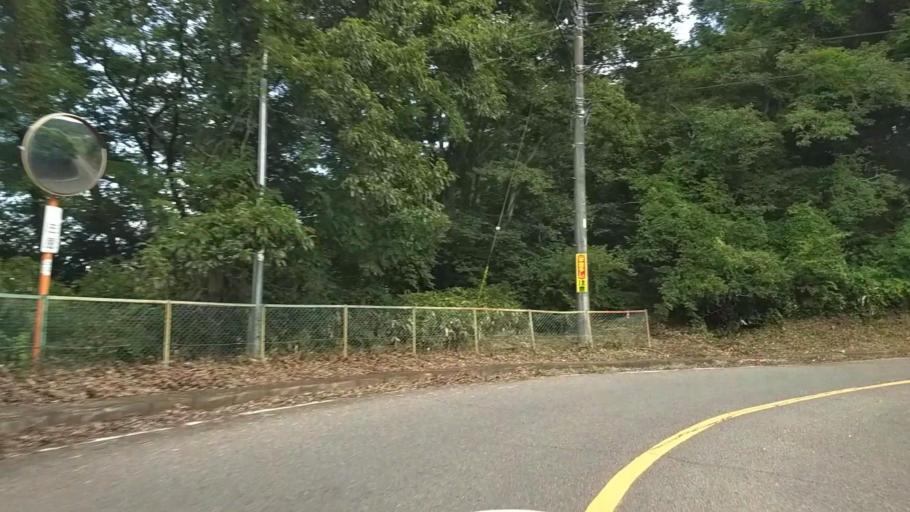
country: JP
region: Yamanashi
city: Uenohara
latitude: 35.6158
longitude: 139.1373
